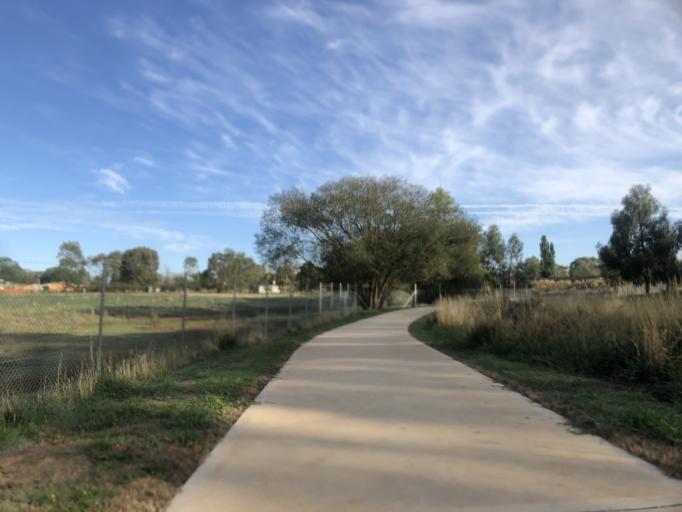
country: AU
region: New South Wales
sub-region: Orange Municipality
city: Orange
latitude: -33.3003
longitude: 149.0921
